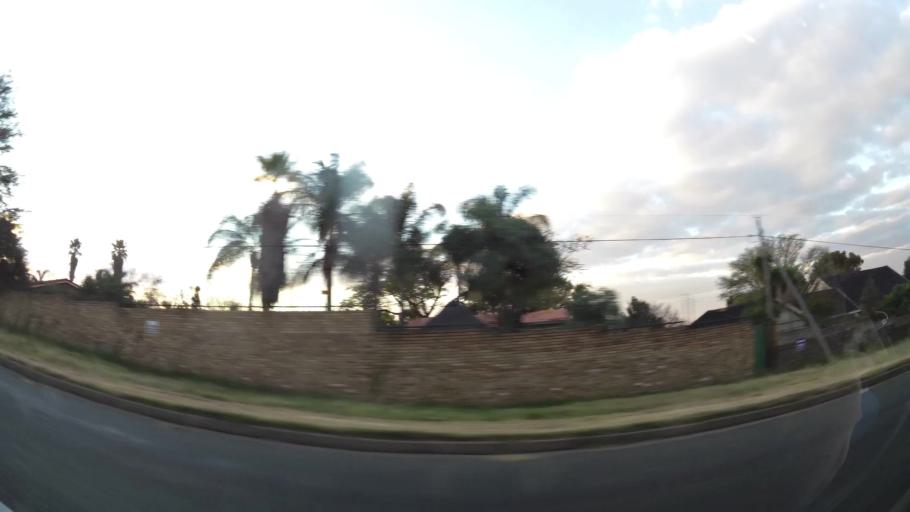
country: ZA
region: Gauteng
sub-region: West Rand District Municipality
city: Krugersdorp
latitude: -26.0757
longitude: 27.7863
